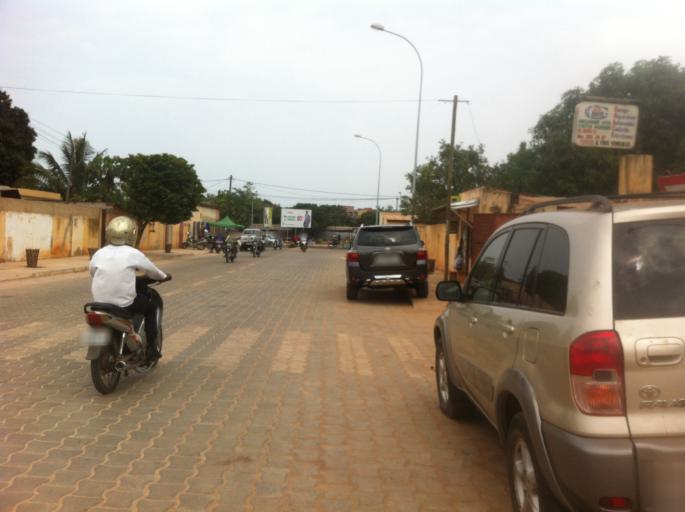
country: TG
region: Maritime
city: Lome
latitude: 6.1857
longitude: 1.2063
